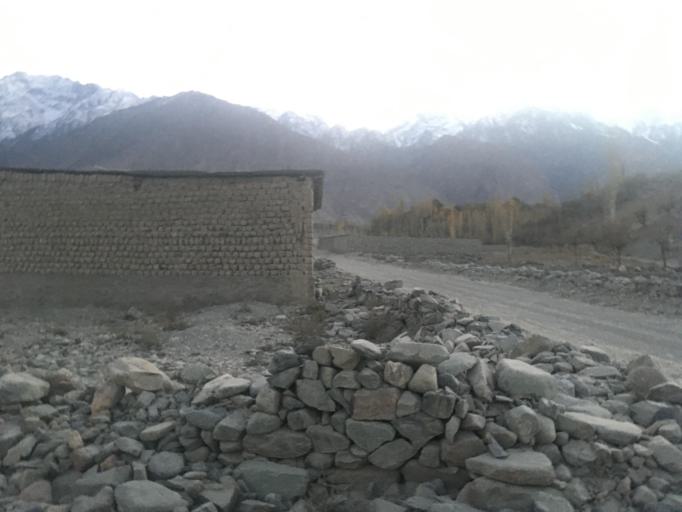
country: PK
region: Gilgit-Baltistan
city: Skardu
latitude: 35.2923
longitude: 75.5687
